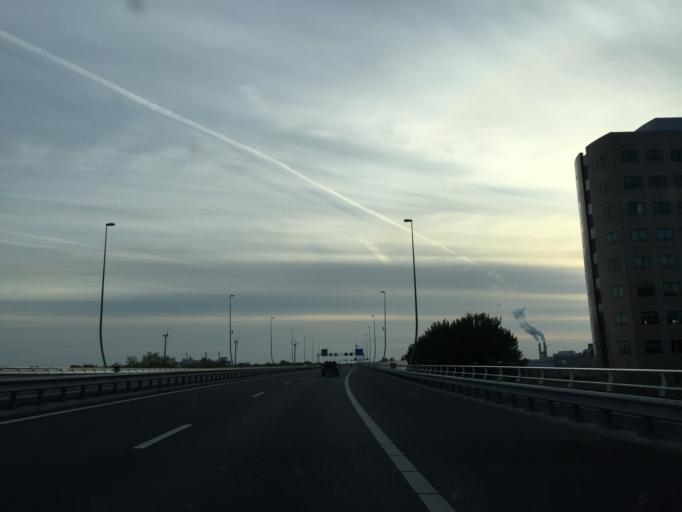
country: NL
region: North Holland
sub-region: Gemeente Zaanstad
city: Zaandam
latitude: 52.3920
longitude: 4.8336
